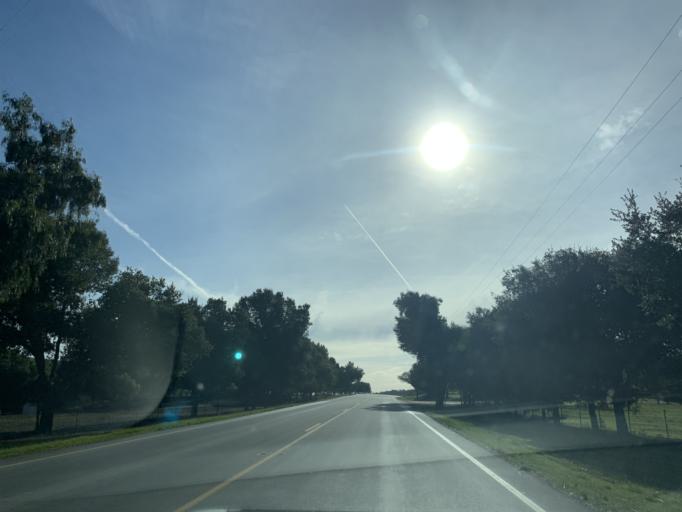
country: US
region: California
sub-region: San Benito County
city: Ridgemark
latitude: 36.7620
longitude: -121.2970
